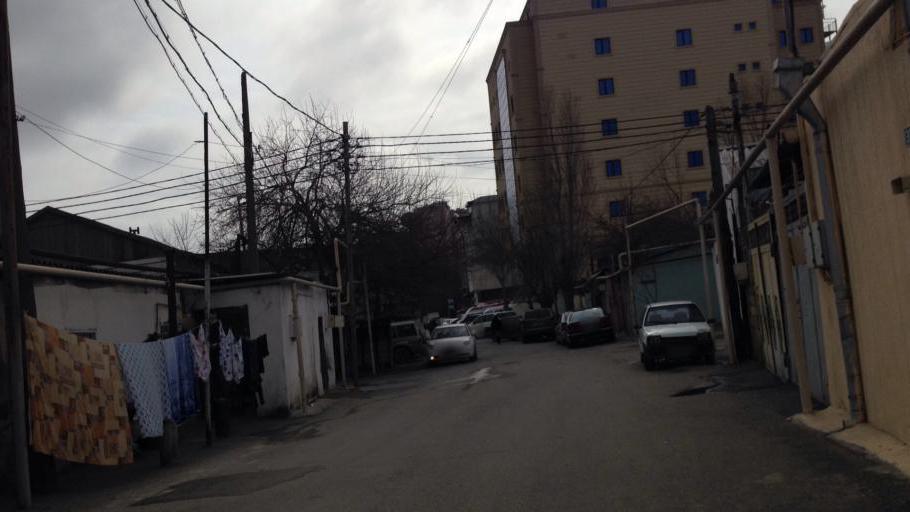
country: AZ
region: Baki
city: Bilajari
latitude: 40.3990
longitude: 49.8284
